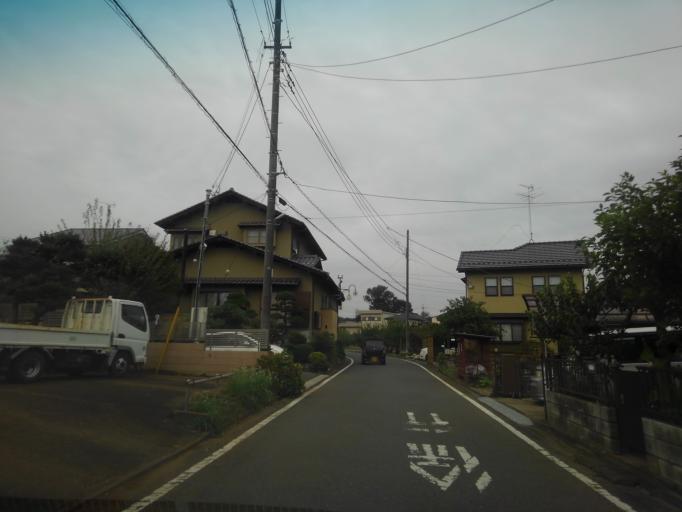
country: JP
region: Saitama
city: Sayama
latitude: 35.7910
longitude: 139.3798
